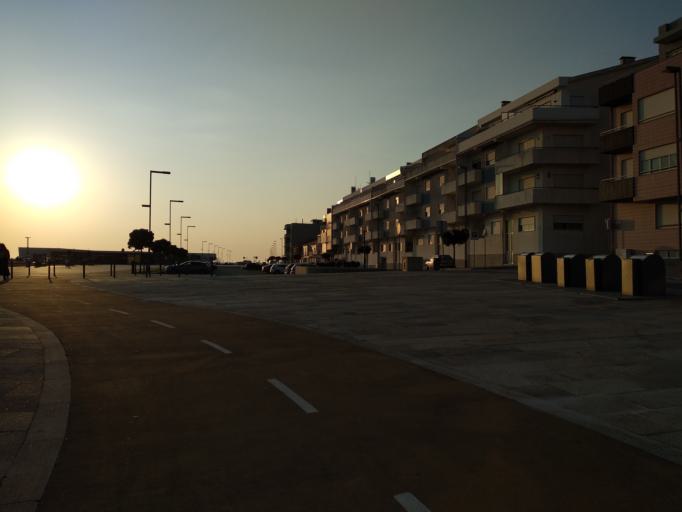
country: PT
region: Viana do Castelo
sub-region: Caminha
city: Vila Praia de Ancora
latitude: 41.8157
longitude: -8.8667
